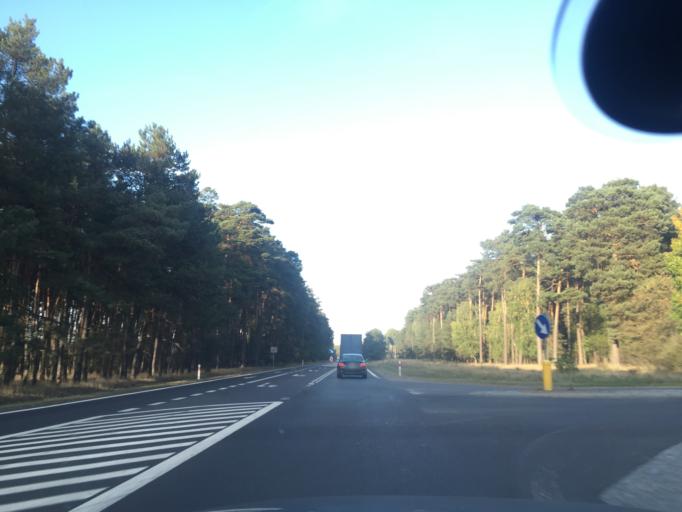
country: PL
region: Kujawsko-Pomorskie
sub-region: Powiat torunski
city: Wielka Nieszawka
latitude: 52.9544
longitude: 18.5306
